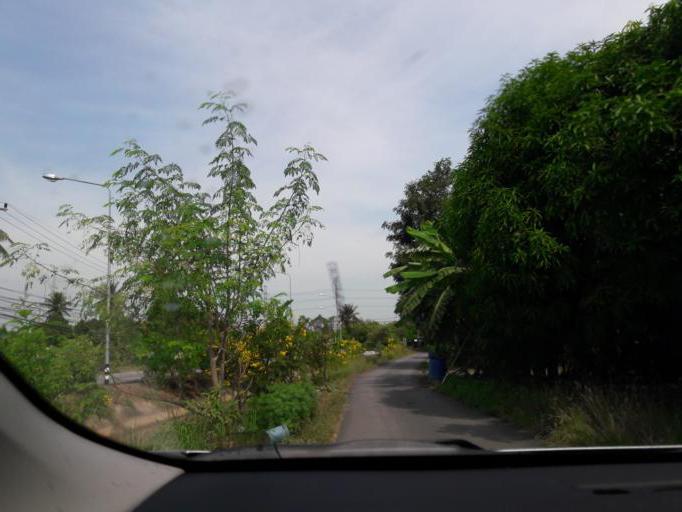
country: TH
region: Ang Thong
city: Ang Thong
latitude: 14.5768
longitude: 100.4751
